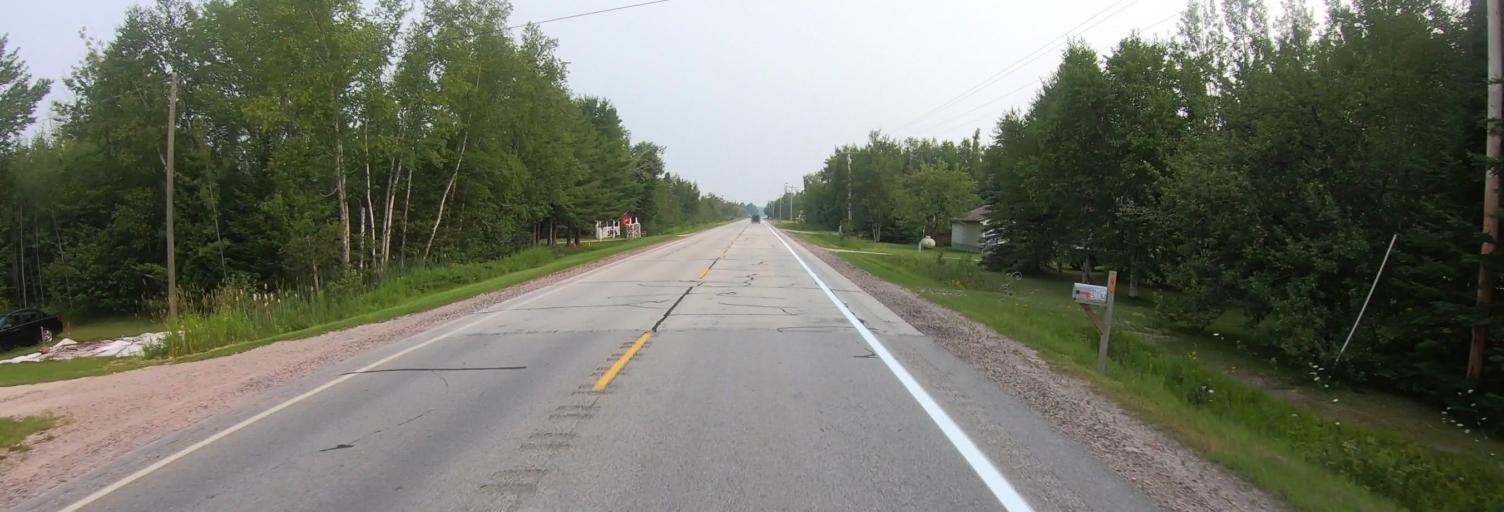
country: US
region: Michigan
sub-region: Luce County
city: Newberry
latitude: 46.5832
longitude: -85.0367
